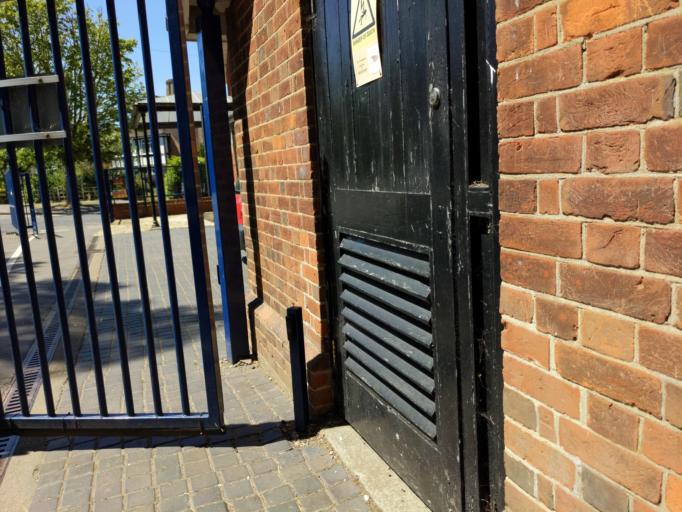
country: GB
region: England
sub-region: Greater London
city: Bromley
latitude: 51.3743
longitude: 0.0164
